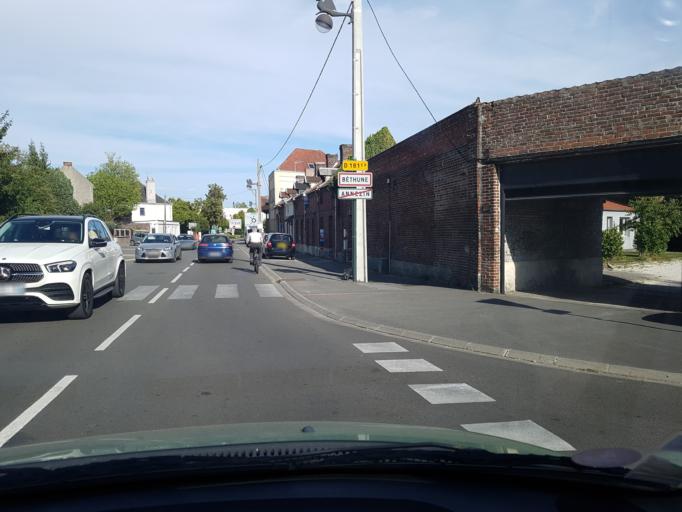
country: FR
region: Nord-Pas-de-Calais
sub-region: Departement du Pas-de-Calais
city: Bethune
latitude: 50.5392
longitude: 2.6253
